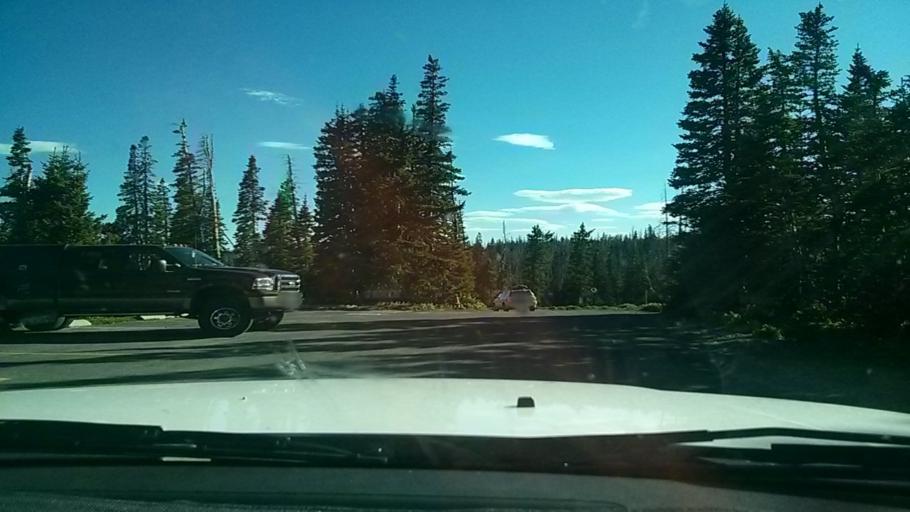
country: US
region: Utah
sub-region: Iron County
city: Parowan
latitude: 37.6125
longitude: -112.8311
